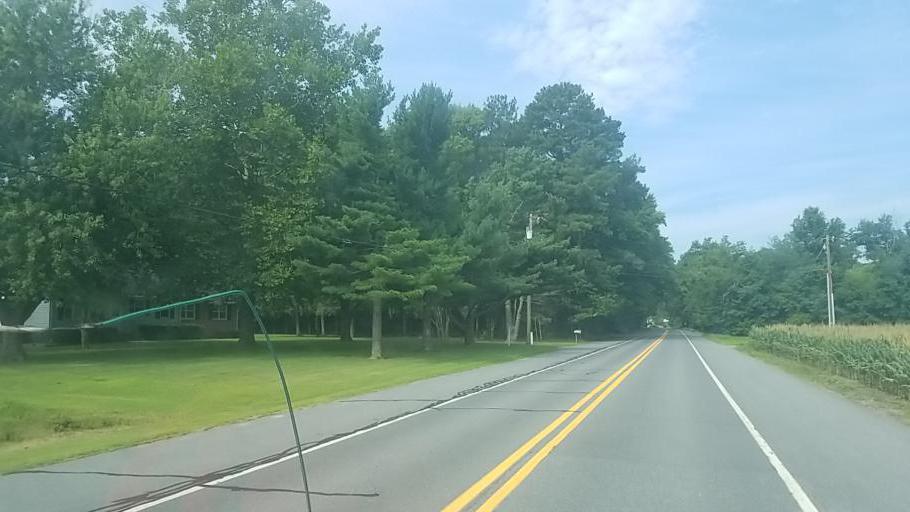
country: US
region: Delaware
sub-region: Sussex County
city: Long Neck
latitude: 38.5447
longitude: -75.1683
